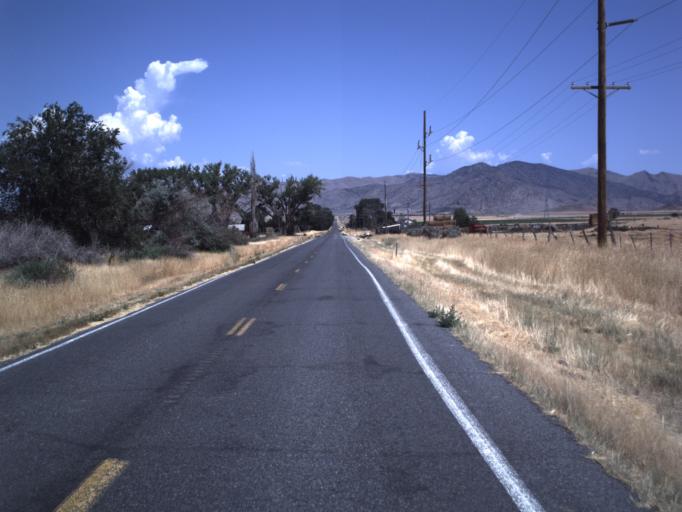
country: US
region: Utah
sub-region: Millard County
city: Delta
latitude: 39.4780
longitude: -112.2688
